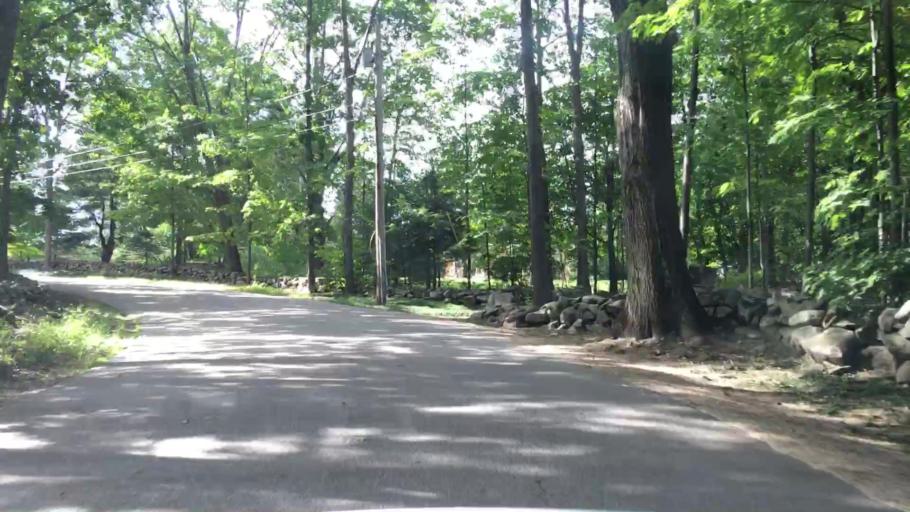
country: US
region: New Hampshire
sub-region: Strafford County
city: Madbury
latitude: 43.1627
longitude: -70.9248
